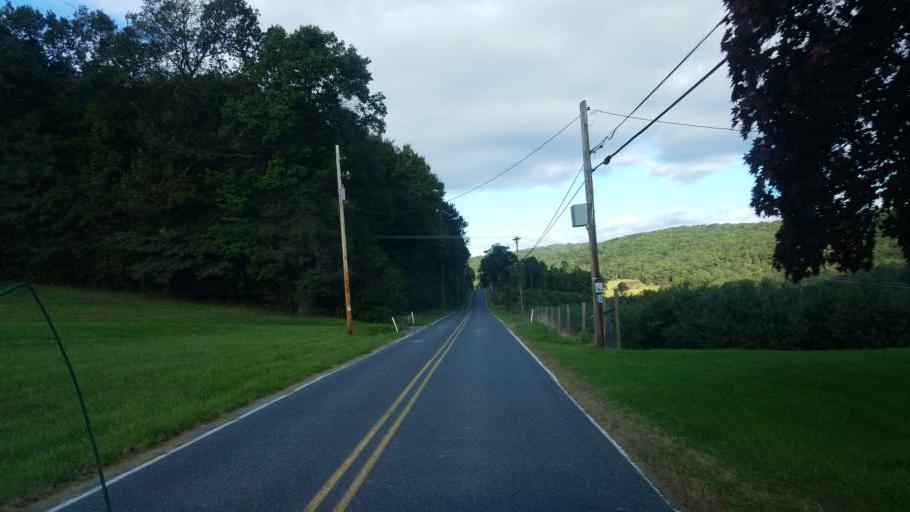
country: US
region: Pennsylvania
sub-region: Adams County
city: Biglerville
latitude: 39.8897
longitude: -77.3702
